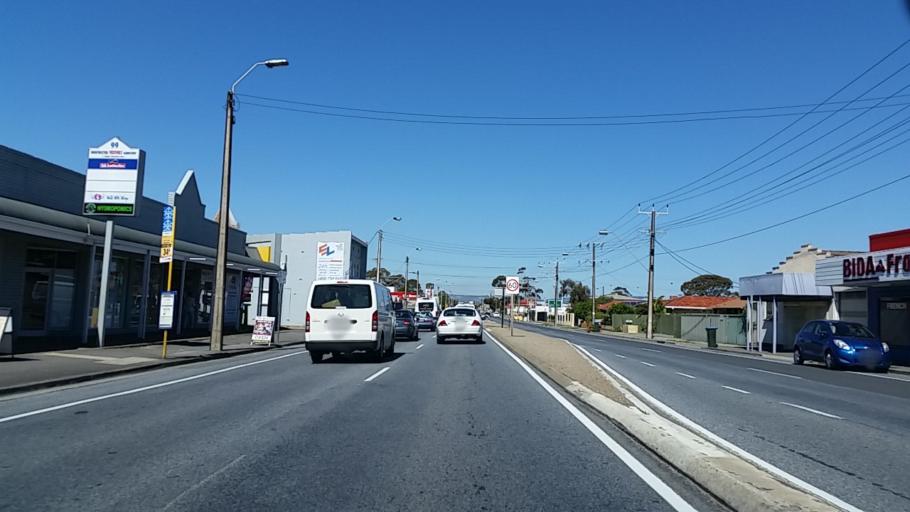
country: AU
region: South Australia
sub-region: Port Adelaide Enfield
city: Alberton
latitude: -34.8517
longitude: 138.5220
